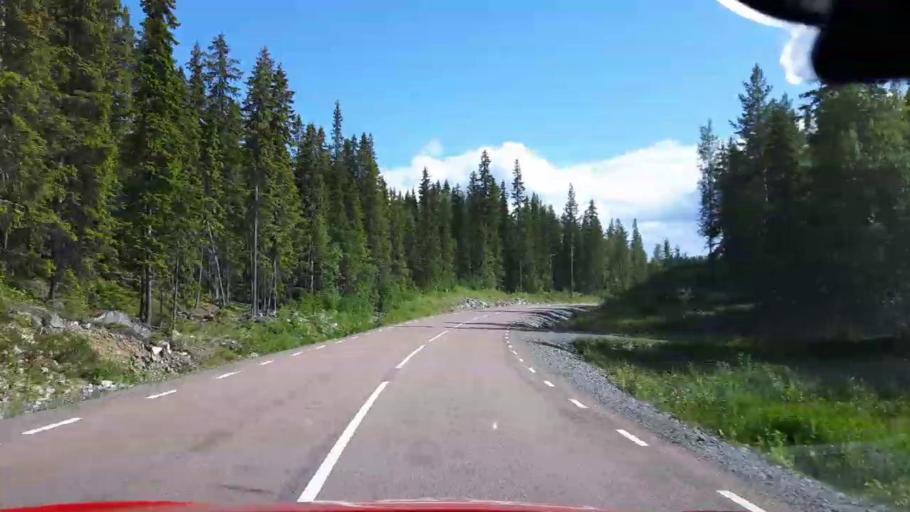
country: SE
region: Jaemtland
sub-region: Krokoms Kommun
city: Valla
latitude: 64.0284
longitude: 14.1975
